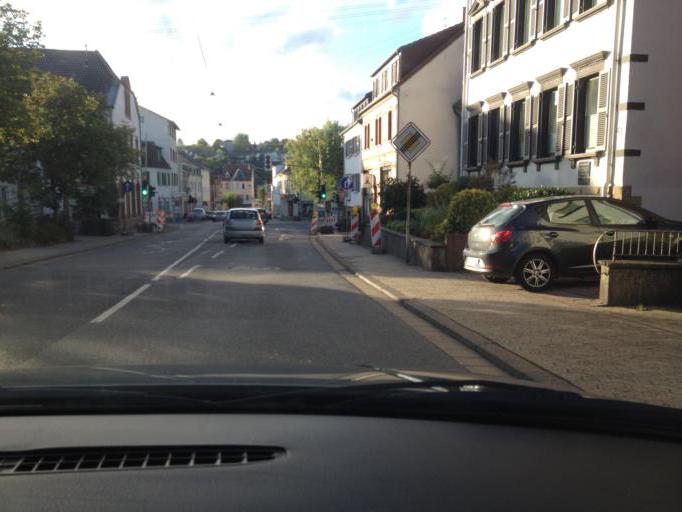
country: DE
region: Saarland
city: Puttlingen
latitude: 49.2883
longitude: 6.8870
